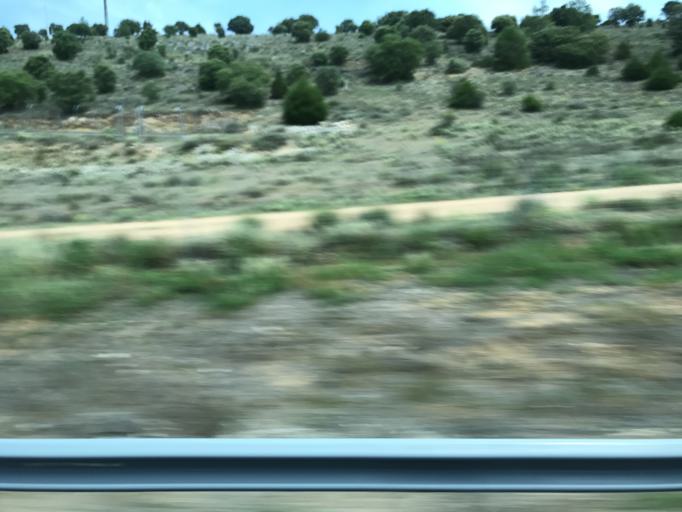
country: ES
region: Castille and Leon
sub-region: Provincia de Burgos
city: Quintanilla de la Mata
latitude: 41.9699
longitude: -3.7780
